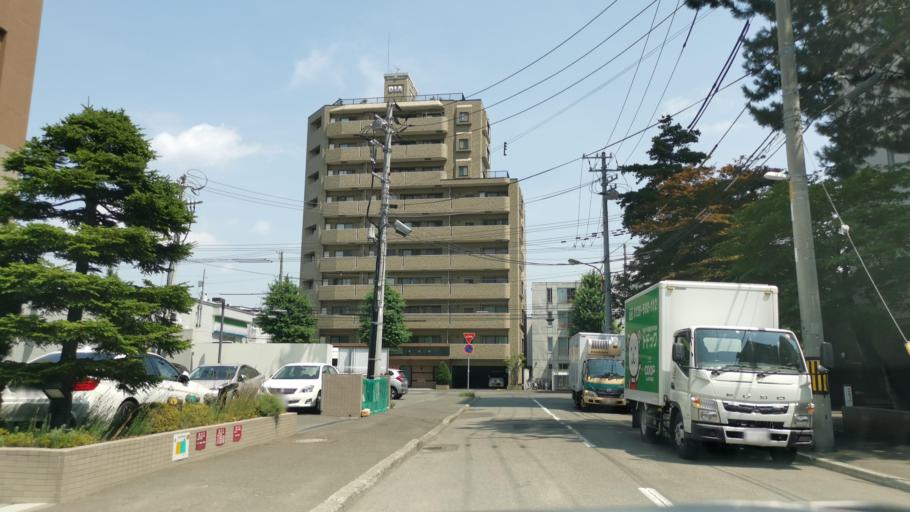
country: JP
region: Hokkaido
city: Sapporo
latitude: 43.0516
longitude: 141.3275
